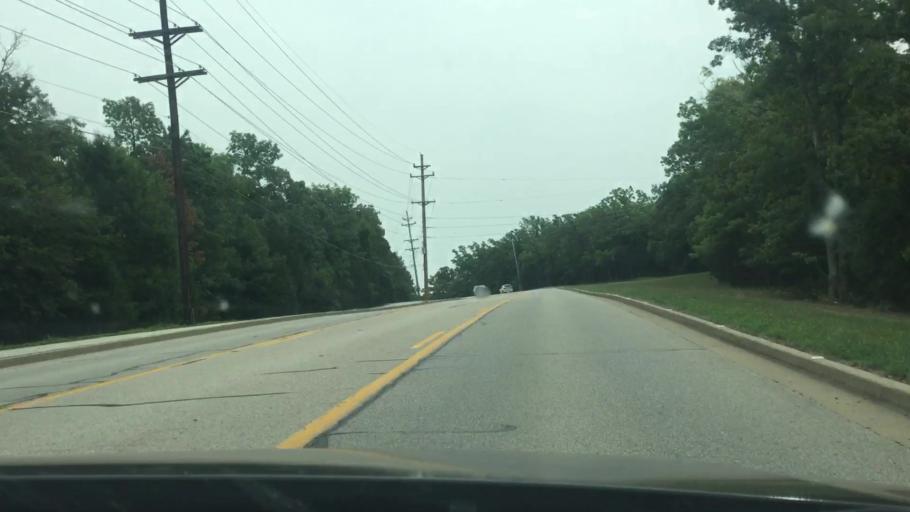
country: US
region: Missouri
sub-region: Camden County
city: Four Seasons
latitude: 38.1921
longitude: -92.7026
